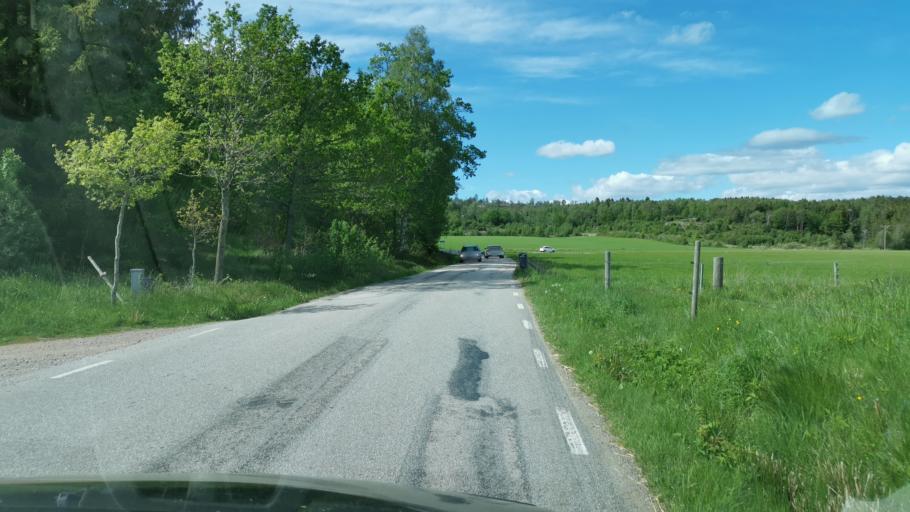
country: SE
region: Vaestra Goetaland
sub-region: Orust
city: Henan
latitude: 58.2777
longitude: 11.5943
